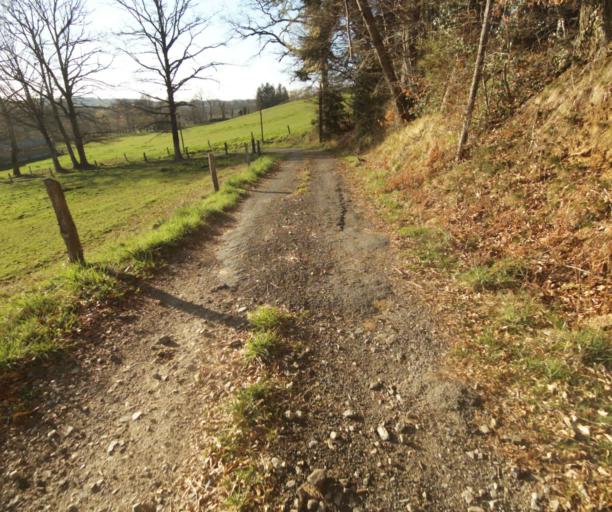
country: FR
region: Limousin
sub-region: Departement de la Correze
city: Seilhac
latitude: 45.3579
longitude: 1.6993
